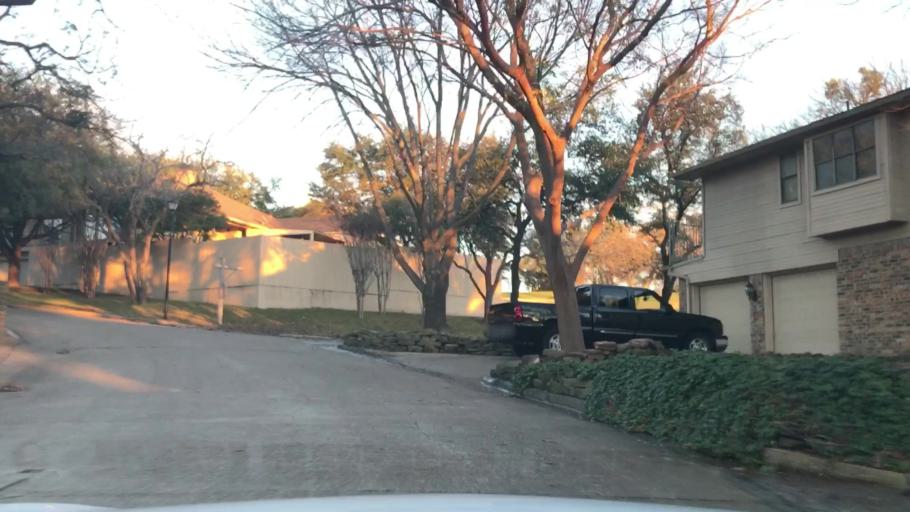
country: US
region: Texas
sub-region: Rockwall County
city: Heath
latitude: 32.8769
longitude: -96.4776
